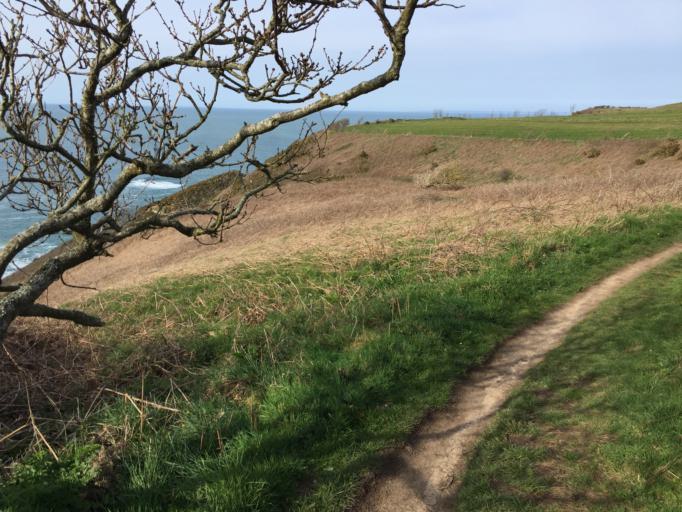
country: JE
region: St Helier
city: Saint Helier
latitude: 49.2490
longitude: -2.1735
